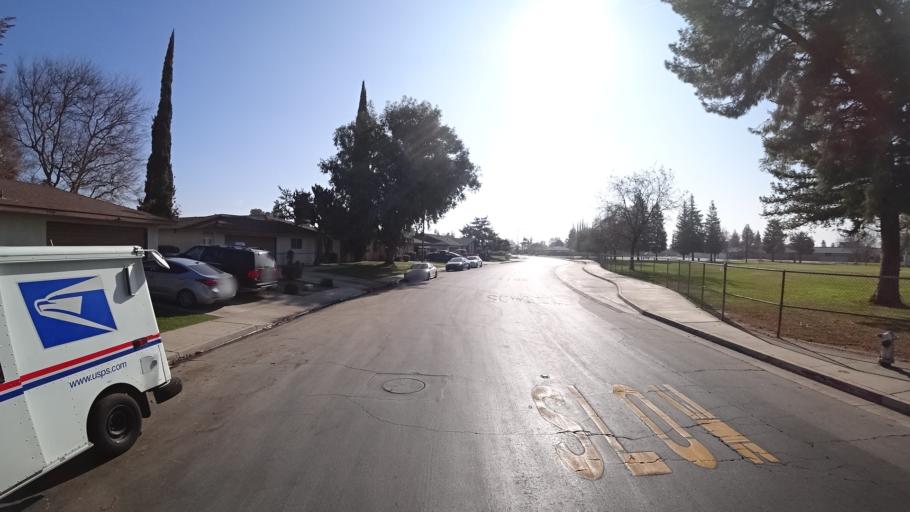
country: US
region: California
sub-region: Kern County
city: Bakersfield
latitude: 35.3348
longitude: -119.0621
